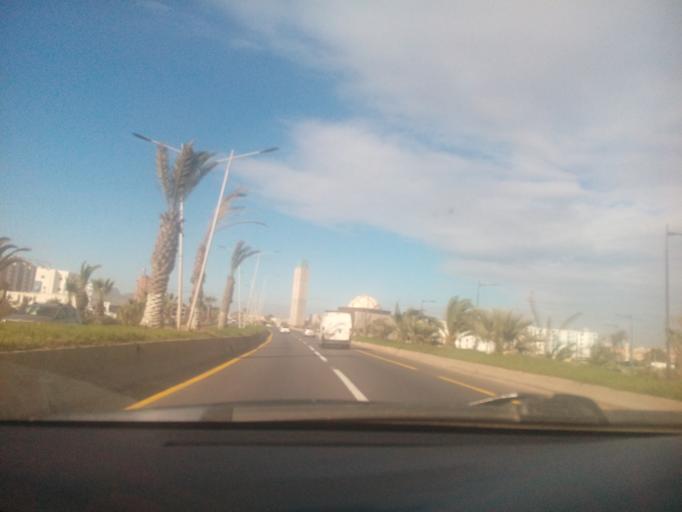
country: DZ
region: Oran
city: Es Senia
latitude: 35.6766
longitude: -0.5985
